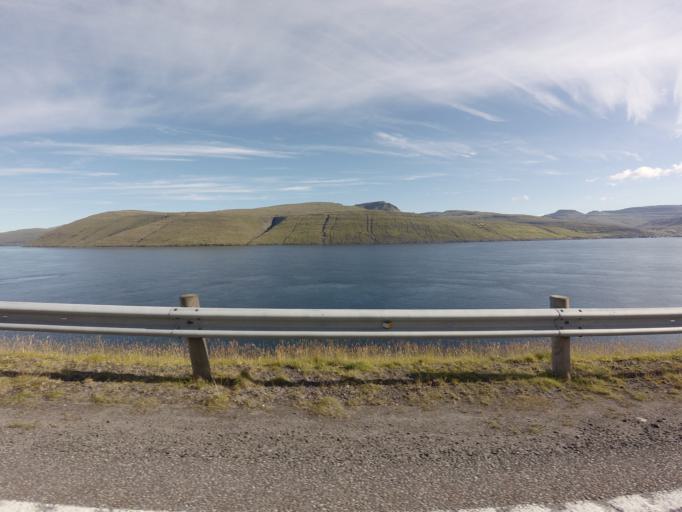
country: FO
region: Streymoy
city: Vestmanna
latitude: 62.1001
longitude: -7.1227
